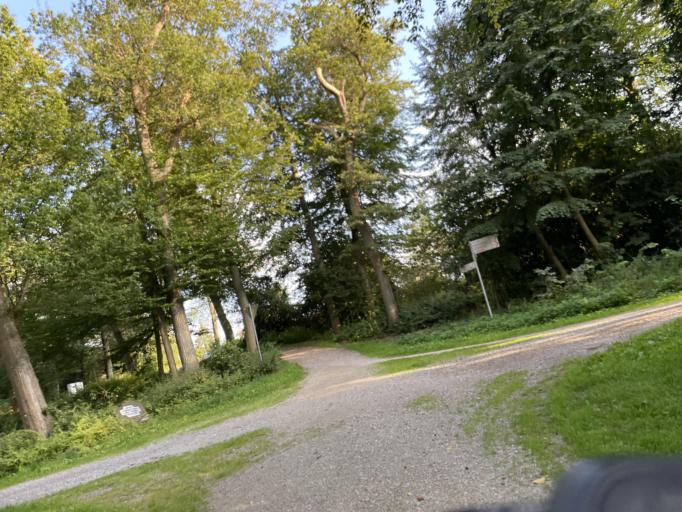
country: DE
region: North Rhine-Westphalia
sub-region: Regierungsbezirk Dusseldorf
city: Essen
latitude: 51.4123
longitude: 7.0525
